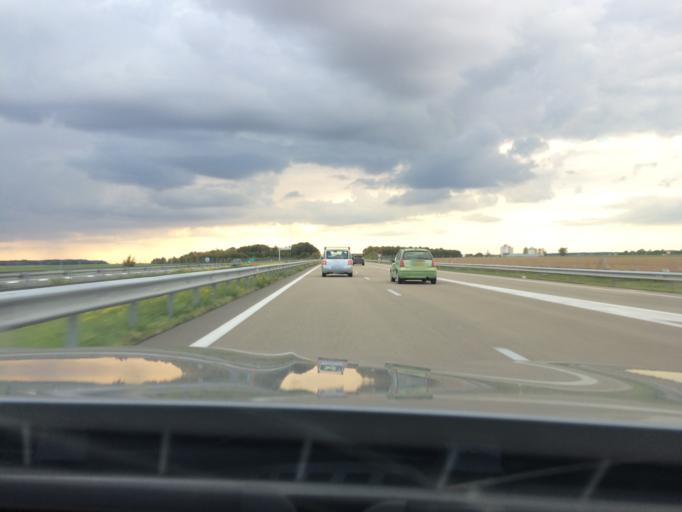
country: FR
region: Ile-de-France
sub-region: Departement de Seine-et-Marne
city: Egreville
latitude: 48.1872
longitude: 2.8253
